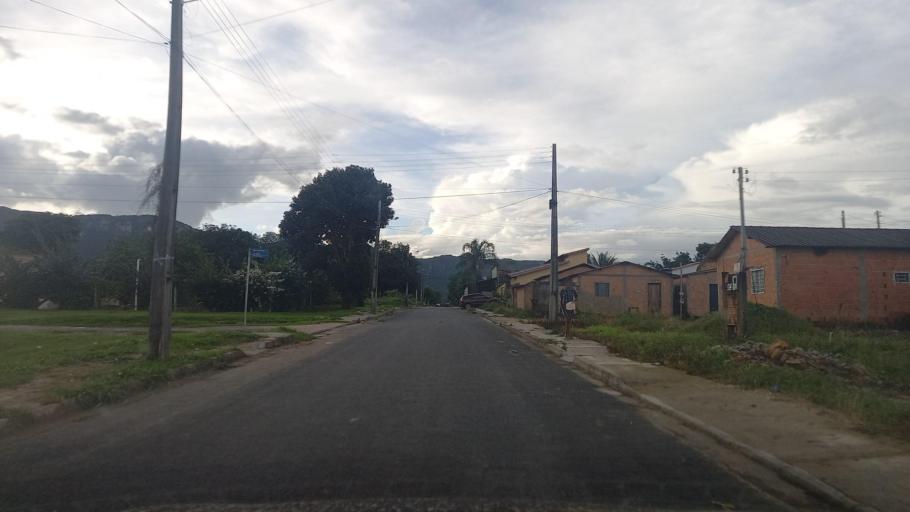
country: BR
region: Goias
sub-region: Cavalcante
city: Cavalcante
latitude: -13.7924
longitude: -47.4546
